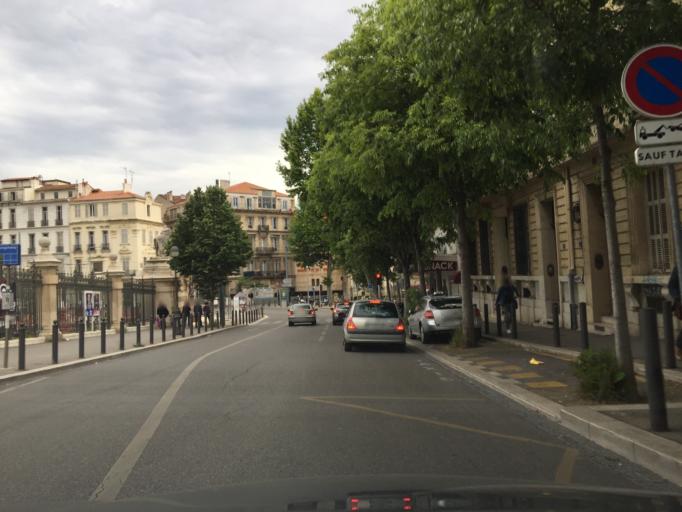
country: FR
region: Provence-Alpes-Cote d'Azur
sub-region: Departement des Bouches-du-Rhone
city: Marseille 04
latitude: 43.3043
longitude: 5.3931
